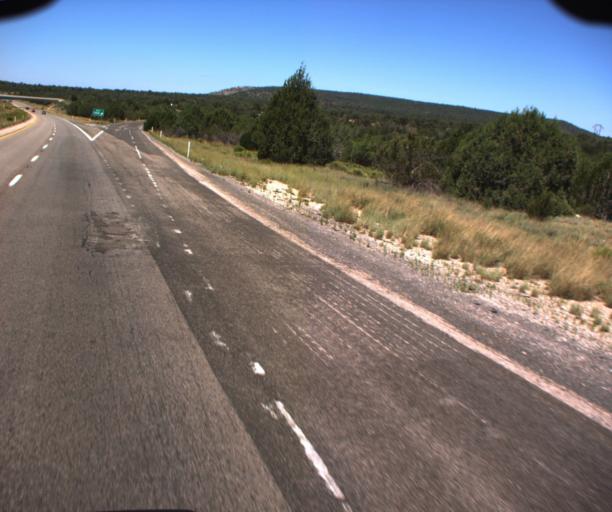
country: US
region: Arizona
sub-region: Mohave County
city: Peach Springs
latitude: 35.2911
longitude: -113.0819
